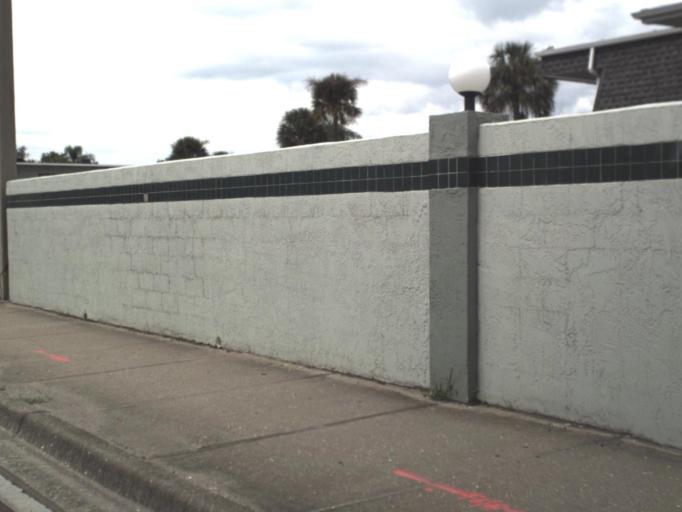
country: US
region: Florida
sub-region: Sarasota County
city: South Gate Ridge
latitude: 27.2989
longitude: -82.5006
